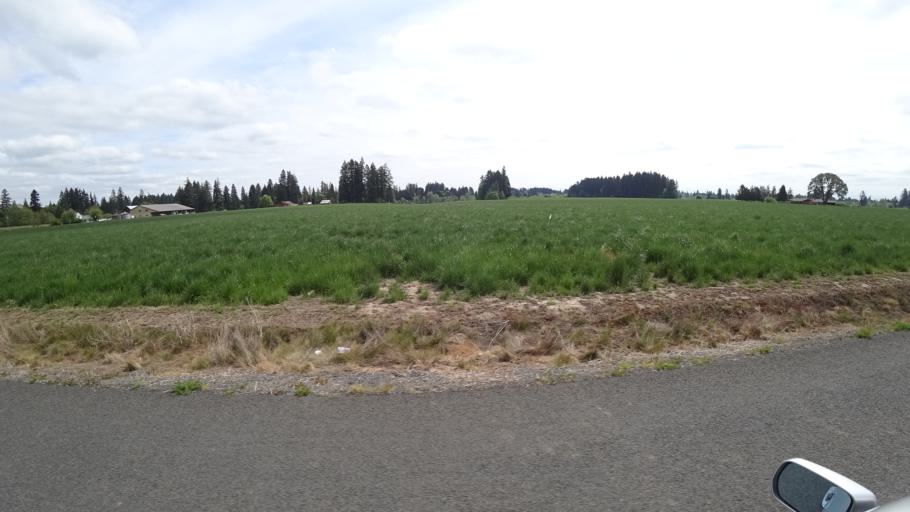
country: US
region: Oregon
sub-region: Washington County
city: Hillsboro
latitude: 45.5417
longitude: -123.0129
